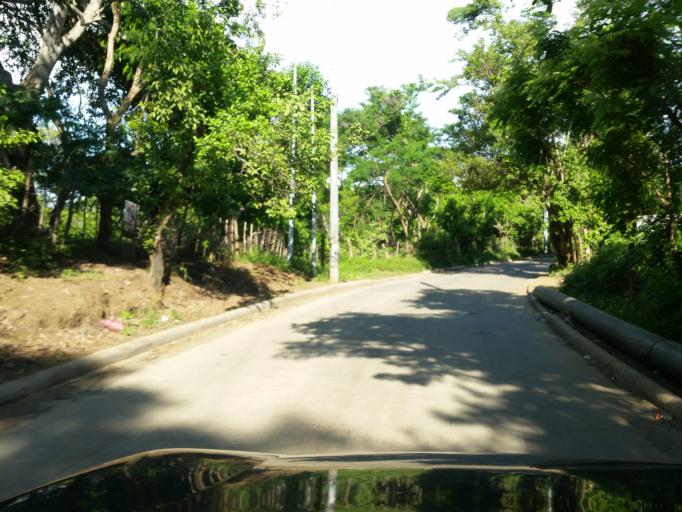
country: NI
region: Managua
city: Managua
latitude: 12.1013
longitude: -86.2171
